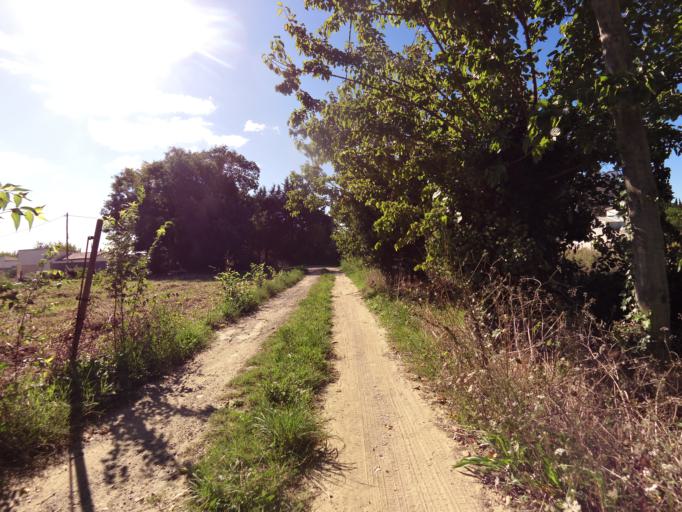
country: FR
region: Languedoc-Roussillon
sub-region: Departement du Gard
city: Aigues-Vives
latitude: 43.7430
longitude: 4.1699
